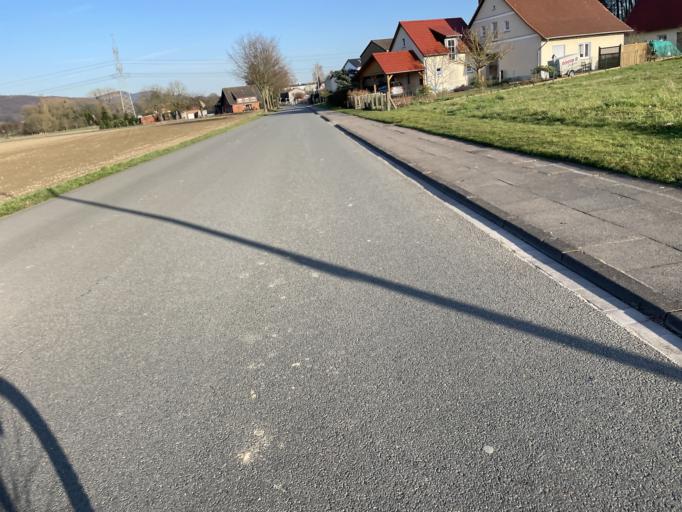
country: DE
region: North Rhine-Westphalia
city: Porta Westfalica
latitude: 52.2259
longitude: 8.9646
